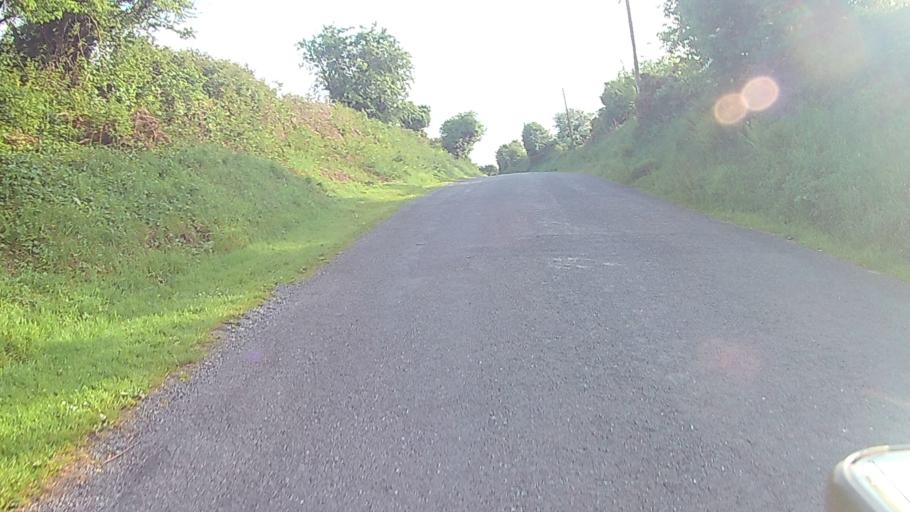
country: IE
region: Munster
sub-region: County Cork
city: Cork
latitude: 51.9708
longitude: -8.4653
